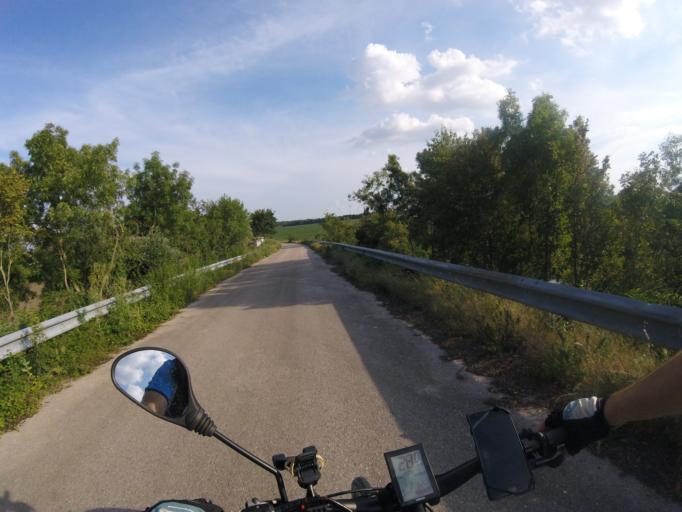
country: AT
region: Lower Austria
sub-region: Politischer Bezirk Baden
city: Trumau
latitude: 47.9710
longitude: 16.3695
